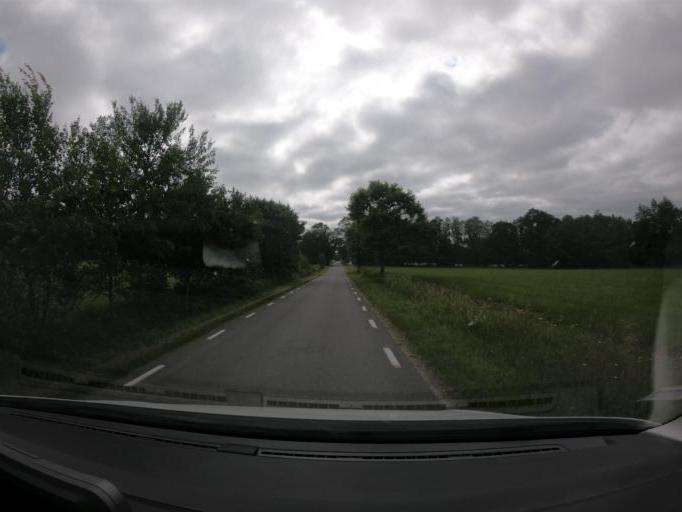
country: SE
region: Skane
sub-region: Hassleholms Kommun
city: Sosdala
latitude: 56.1179
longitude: 13.6396
